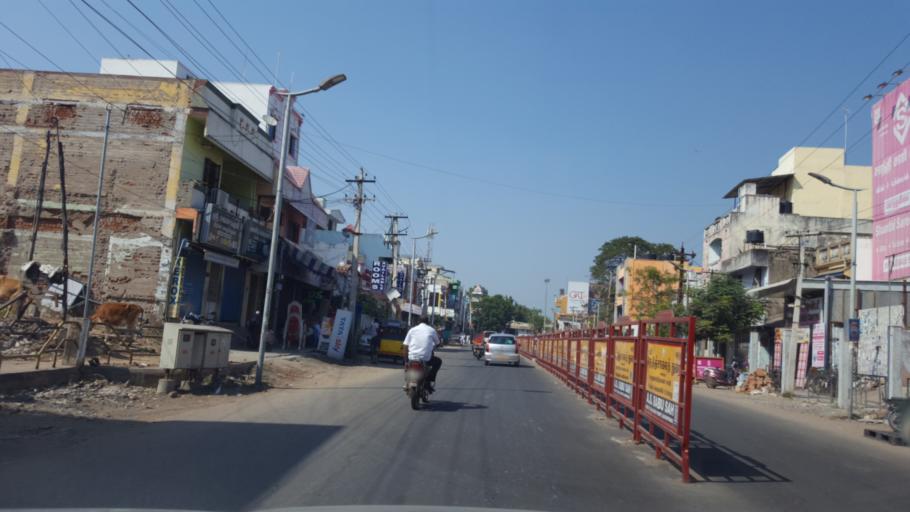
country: IN
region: Tamil Nadu
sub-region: Kancheepuram
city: Kanchipuram
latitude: 12.8416
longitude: 79.7012
